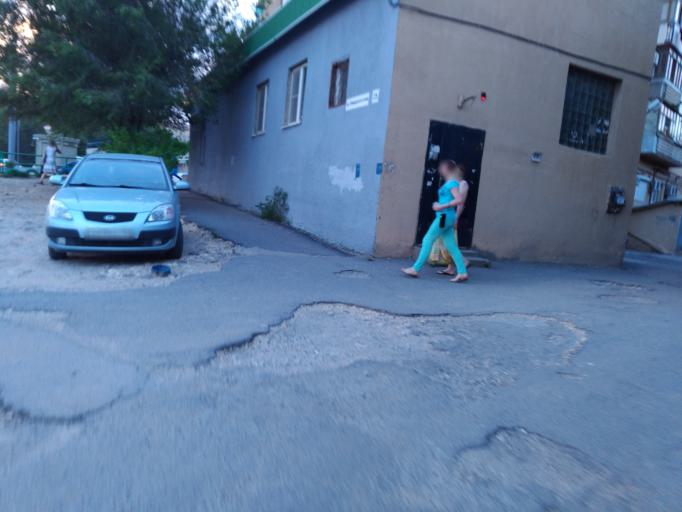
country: RU
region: Volgograd
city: Volgograd
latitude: 48.6739
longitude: 44.4445
